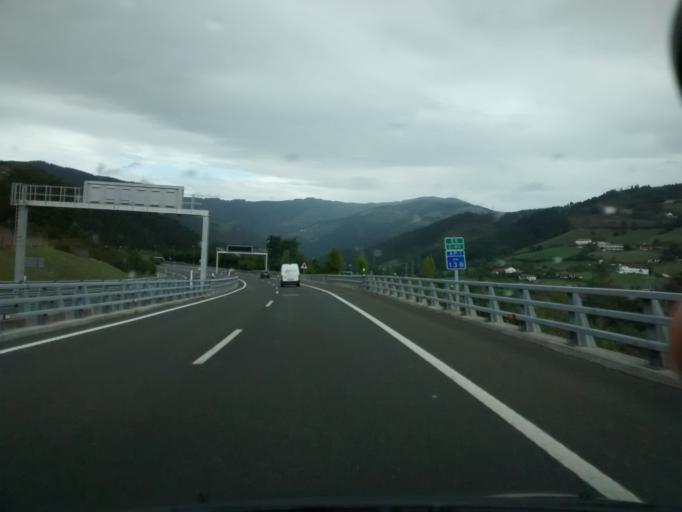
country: ES
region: Basque Country
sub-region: Provincia de Guipuzcoa
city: Bergara
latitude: 43.1278
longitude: -2.4261
